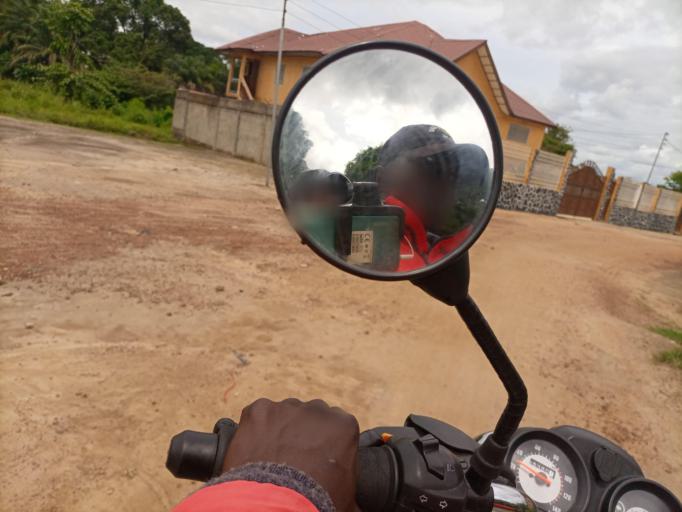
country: SL
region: Southern Province
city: Bo
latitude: 7.9710
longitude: -11.7236
